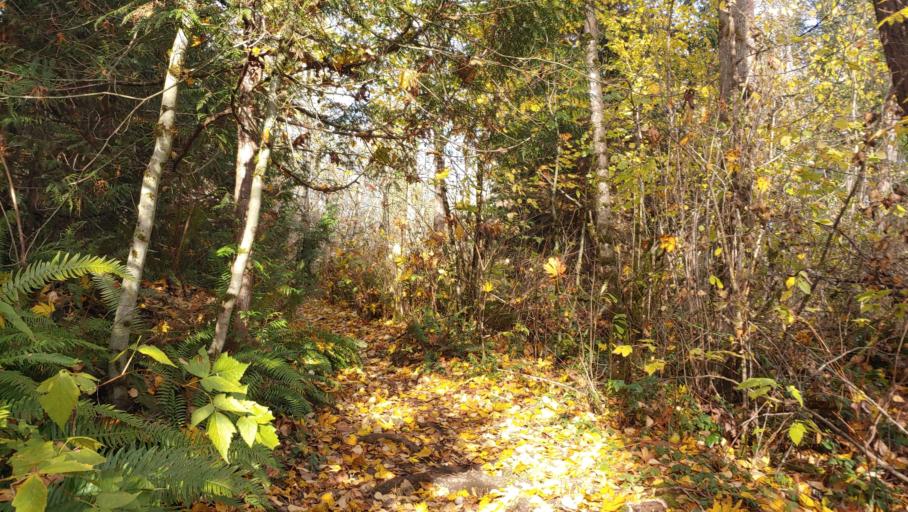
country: US
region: Washington
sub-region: King County
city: Fairwood
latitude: 47.4508
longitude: -122.1648
